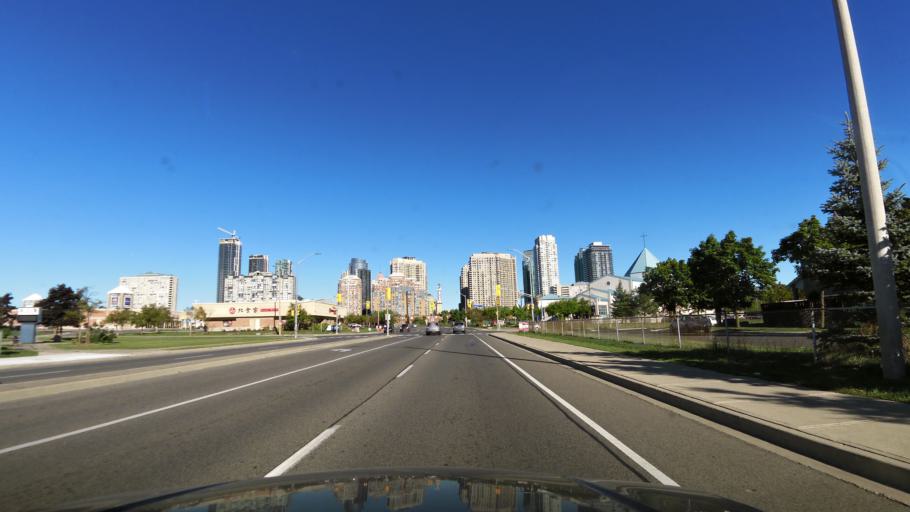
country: CA
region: Ontario
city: Mississauga
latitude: 43.5829
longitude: -79.6353
